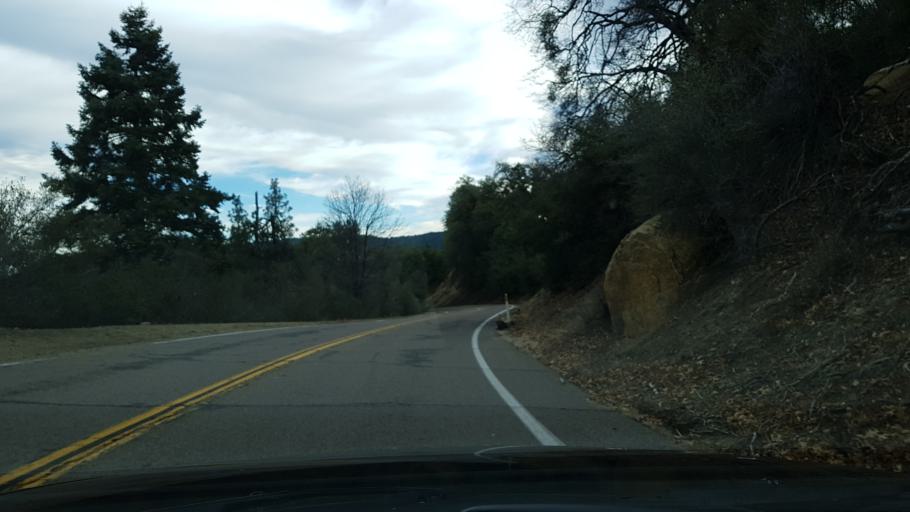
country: US
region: California
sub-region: Riverside County
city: Aguanga
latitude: 33.3479
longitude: -116.8713
